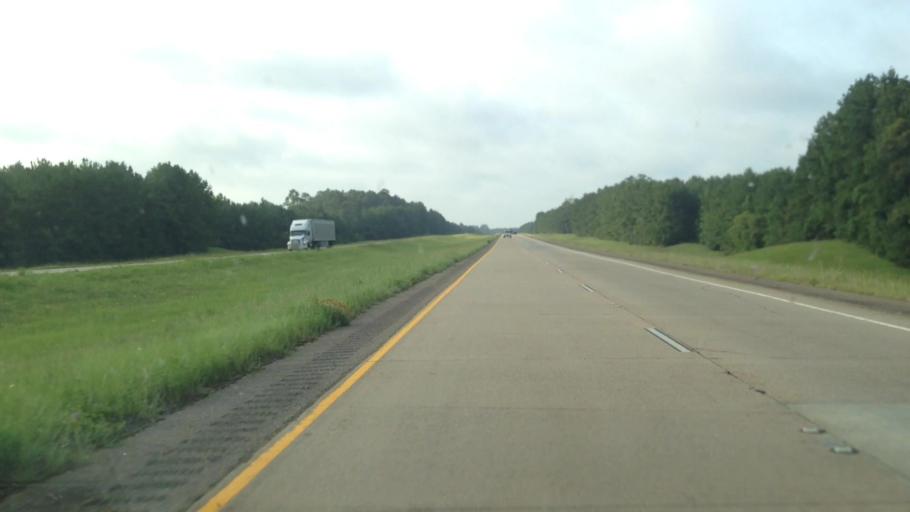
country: US
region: Louisiana
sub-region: Rapides Parish
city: Lecompte
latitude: 31.0554
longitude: -92.4246
